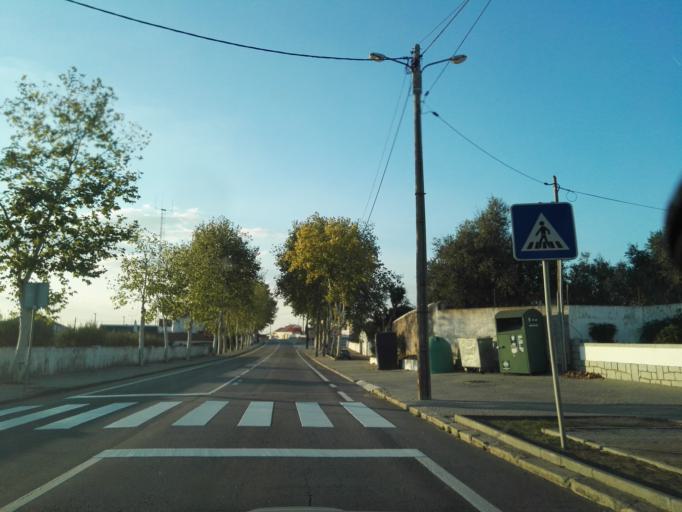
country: PT
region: Evora
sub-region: Mora
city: Mora
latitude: 38.8937
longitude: -8.0192
